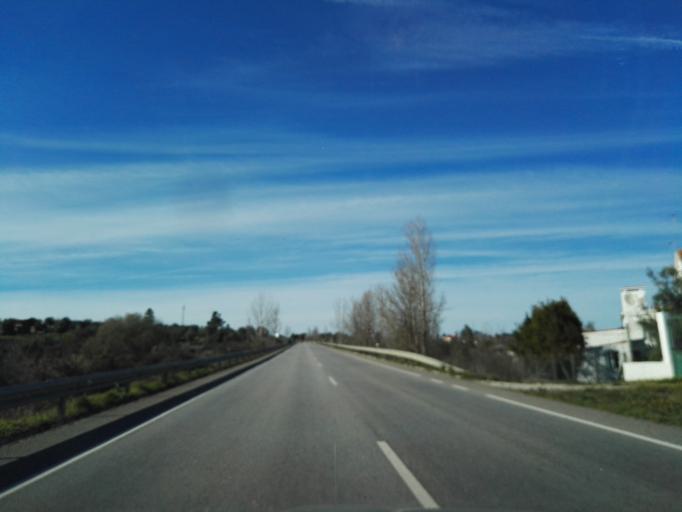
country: PT
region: Santarem
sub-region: Abrantes
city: Alferrarede
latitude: 39.4795
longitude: -8.0857
